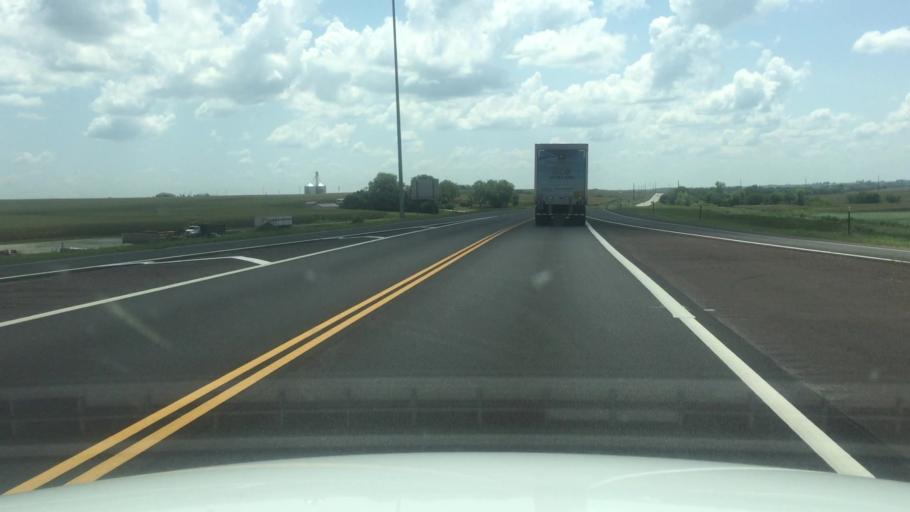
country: US
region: Kansas
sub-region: Nemaha County
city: Sabetha
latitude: 39.8377
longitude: -95.7351
